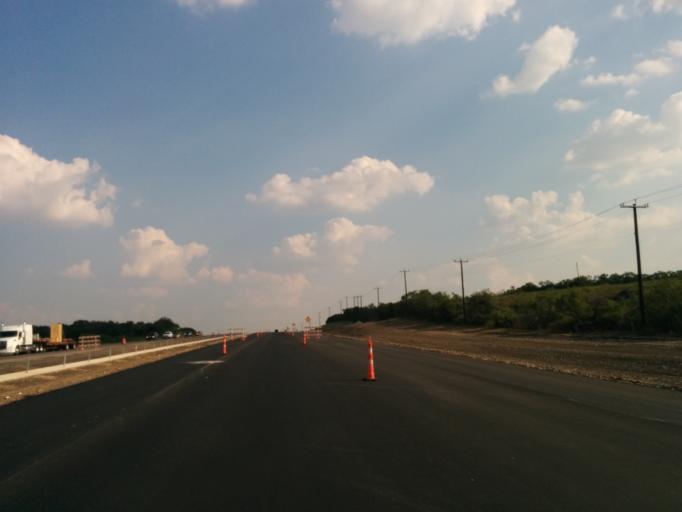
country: US
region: Texas
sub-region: Bexar County
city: Converse
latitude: 29.4741
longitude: -98.2950
